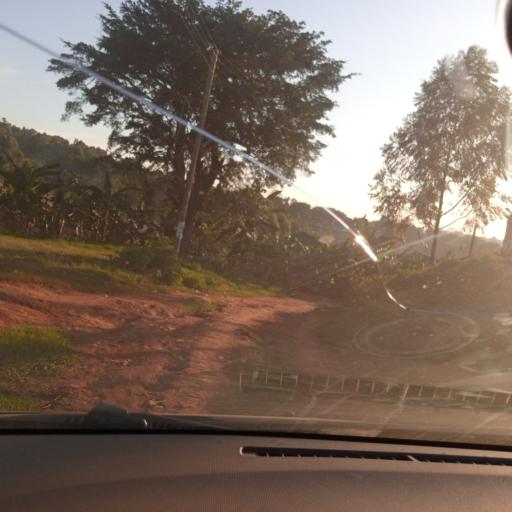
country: UG
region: Central Region
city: Masaka
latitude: -0.3374
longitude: 31.7594
